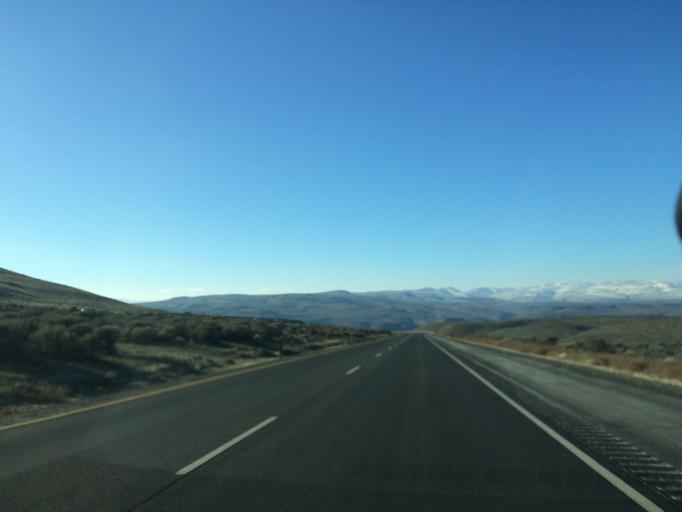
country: US
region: Washington
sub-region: Grant County
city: Quincy
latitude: 47.0067
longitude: -119.9638
